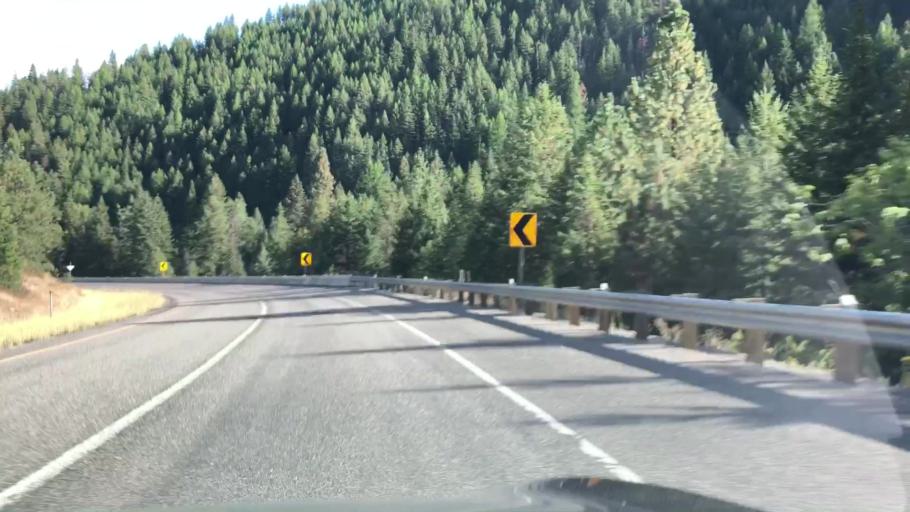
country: US
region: Montana
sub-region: Sanders County
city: Thompson Falls
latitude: 47.3327
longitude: -115.2662
